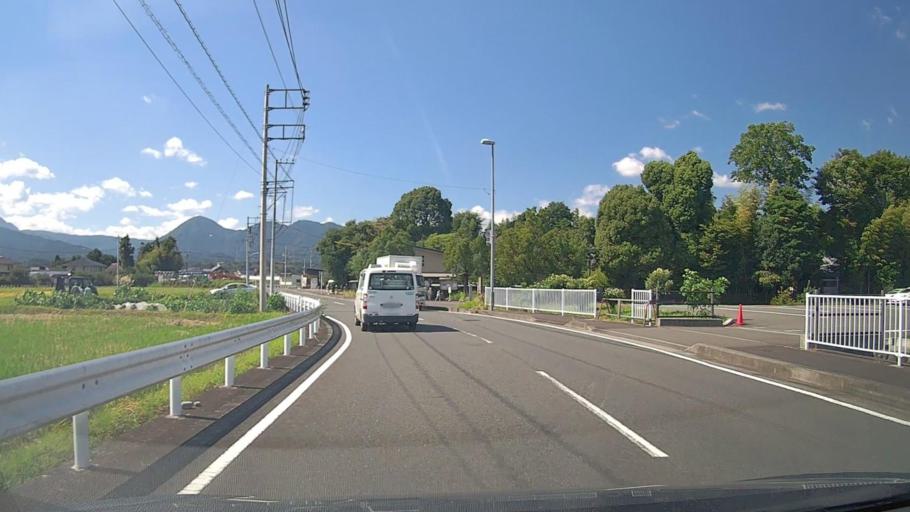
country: JP
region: Kanagawa
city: Odawara
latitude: 35.3426
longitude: 139.1162
